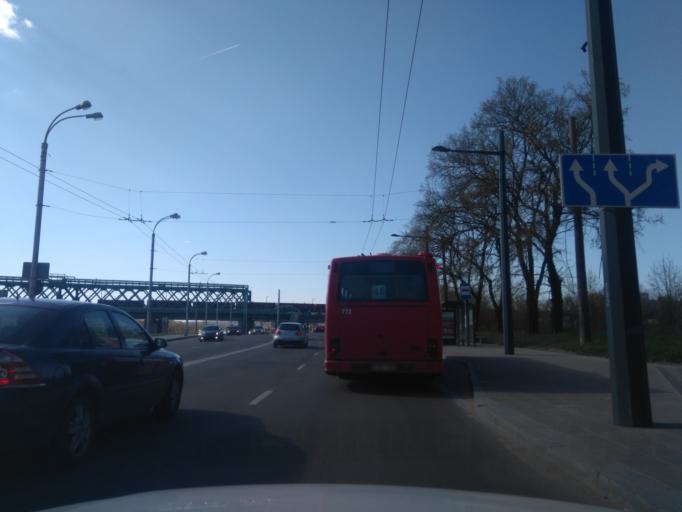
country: LT
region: Kauno apskritis
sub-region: Kaunas
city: Aleksotas
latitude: 54.8816
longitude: 23.9285
